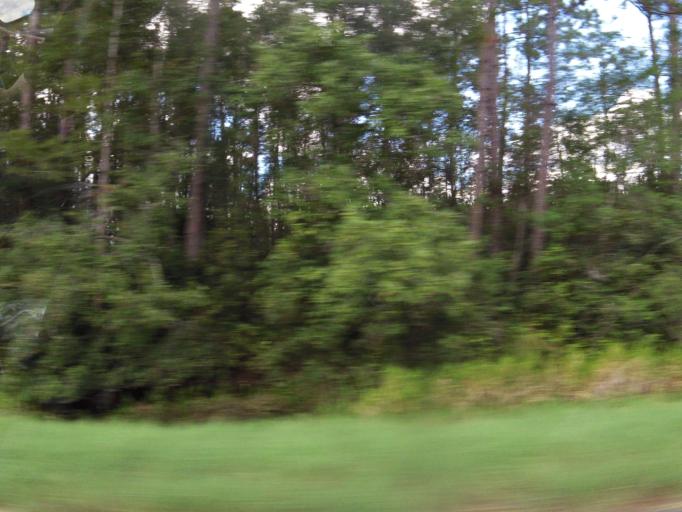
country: US
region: Florida
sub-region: Hamilton County
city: Jasper
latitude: 30.6761
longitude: -82.6920
